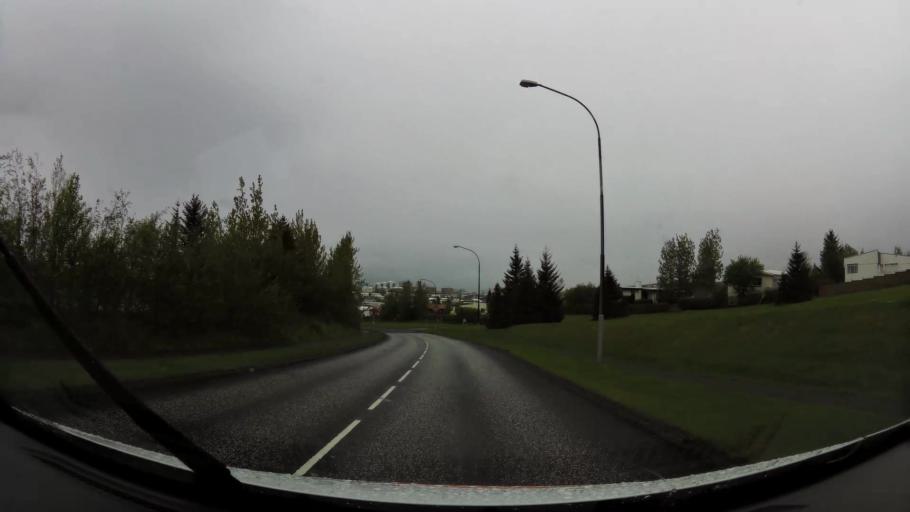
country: IS
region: Capital Region
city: Gardabaer
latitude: 64.0892
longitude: -21.9053
